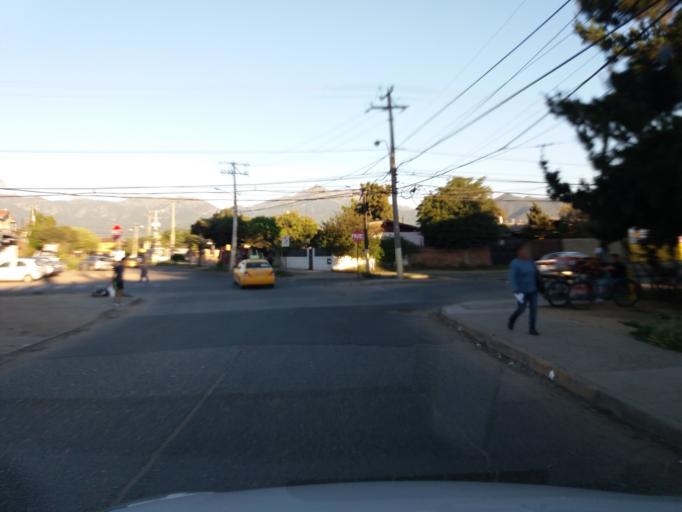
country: CL
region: Valparaiso
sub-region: Provincia de Quillota
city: Quillota
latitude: -32.8811
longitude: -71.2575
